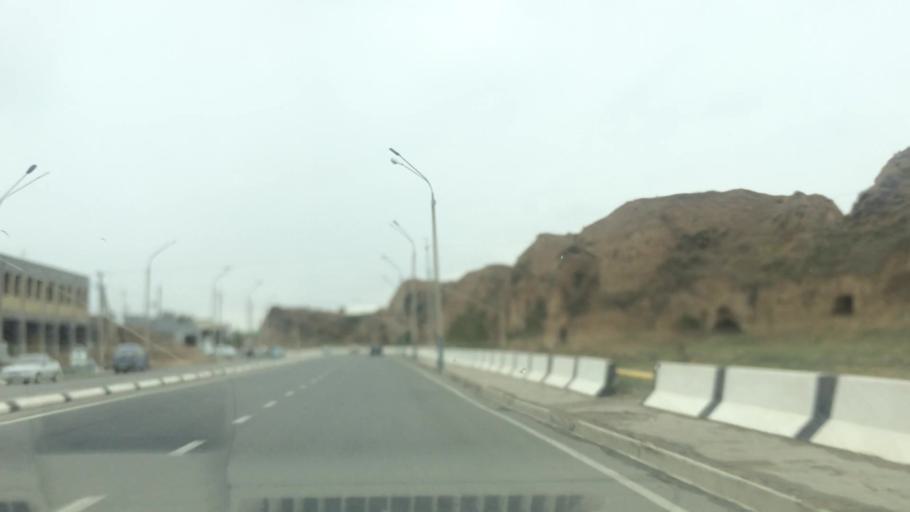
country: UZ
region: Samarqand
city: Samarqand
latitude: 39.6676
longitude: 66.9951
